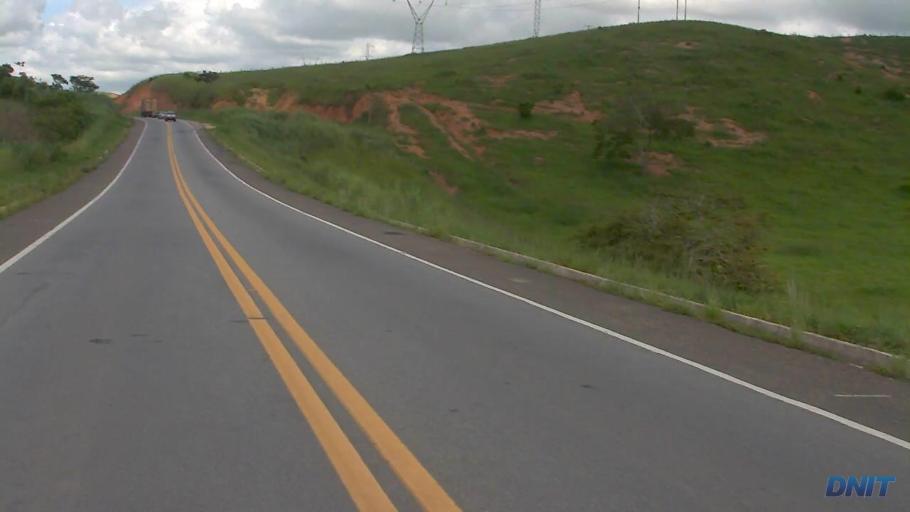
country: BR
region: Minas Gerais
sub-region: Belo Oriente
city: Belo Oriente
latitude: -19.0992
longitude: -42.1979
